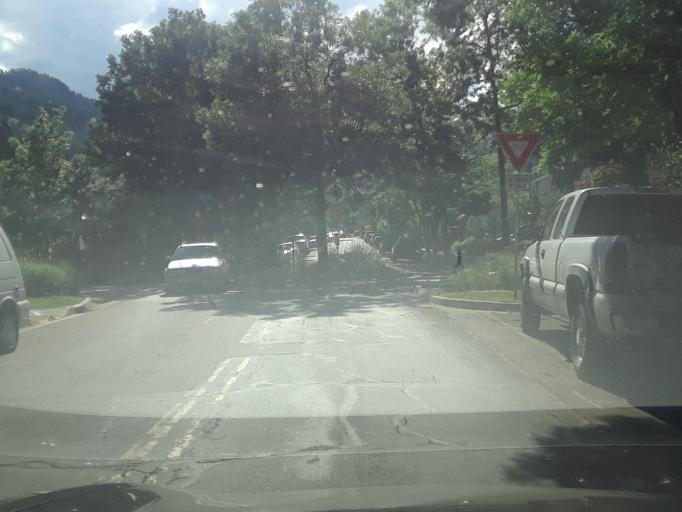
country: US
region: Colorado
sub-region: Boulder County
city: Boulder
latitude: 40.0129
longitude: -105.2888
